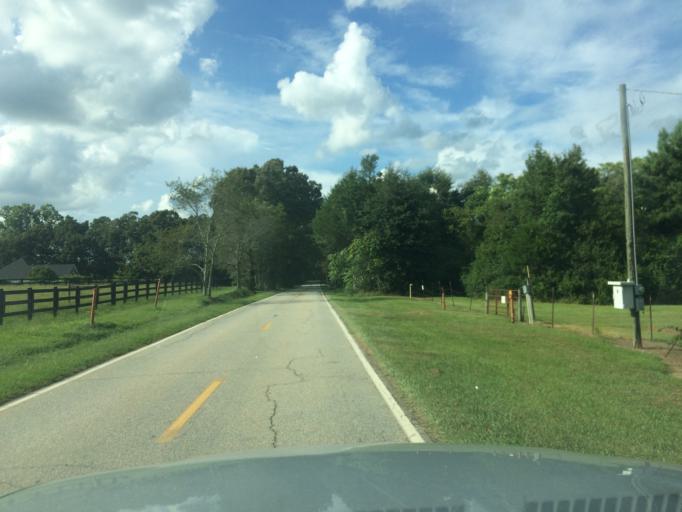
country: US
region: South Carolina
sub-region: Spartanburg County
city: Woodruff
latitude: 34.7766
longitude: -82.1122
